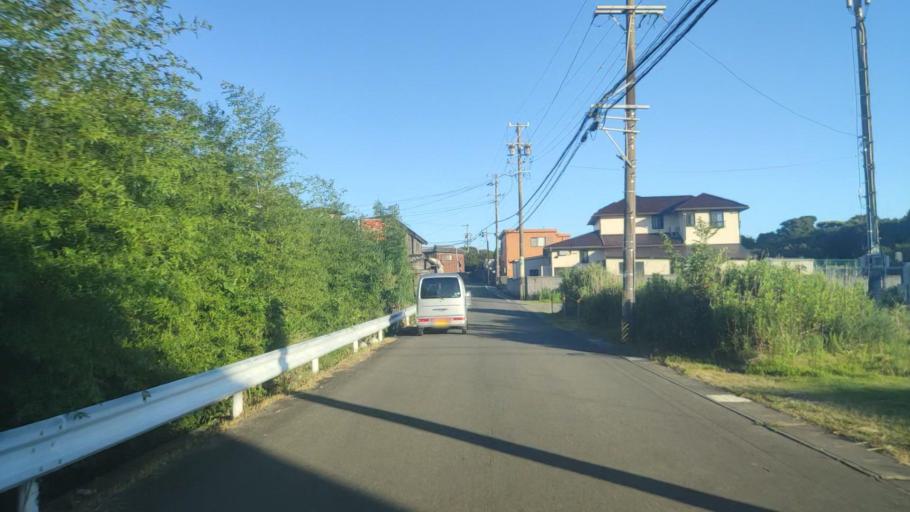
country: JP
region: Mie
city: Toba
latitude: 34.2548
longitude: 136.8425
